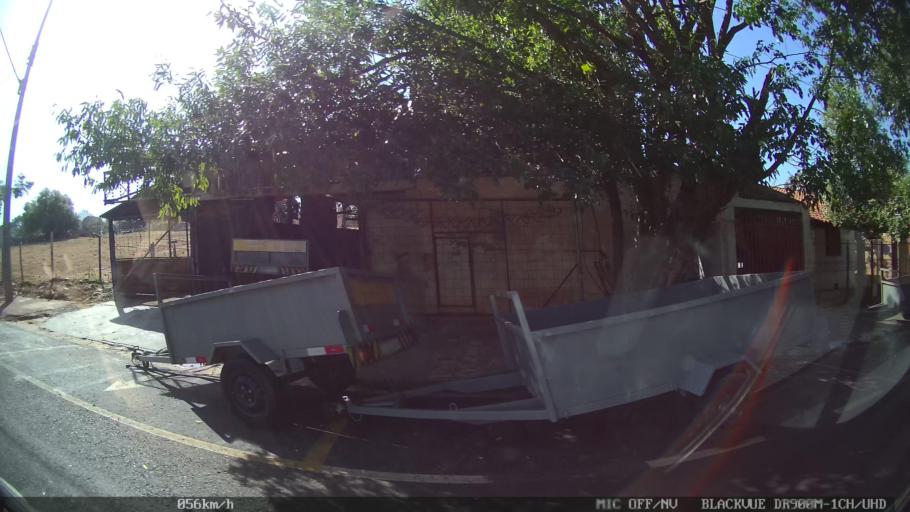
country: BR
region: Sao Paulo
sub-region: Sao Jose Do Rio Preto
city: Sao Jose do Rio Preto
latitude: -20.7907
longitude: -49.4085
